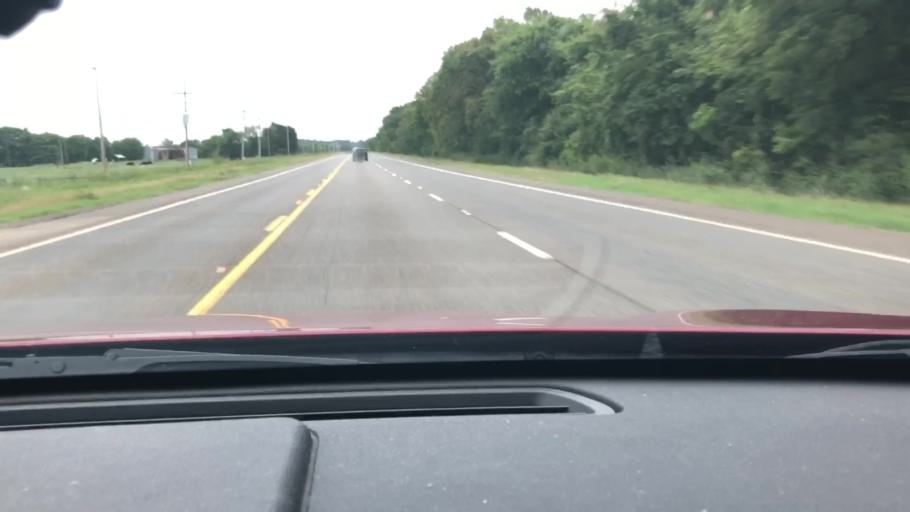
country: US
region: Arkansas
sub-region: Lafayette County
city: Lewisville
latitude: 33.3561
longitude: -93.6557
